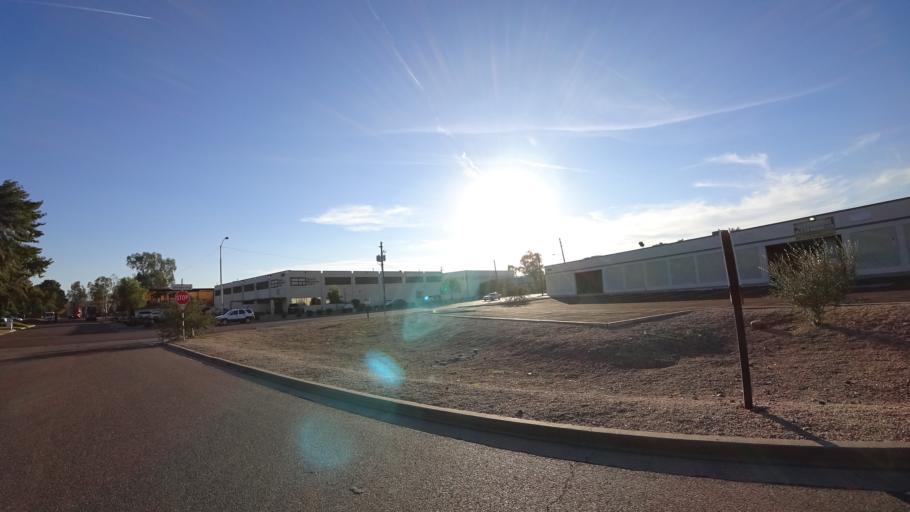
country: US
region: Arizona
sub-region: Maricopa County
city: Phoenix
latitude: 33.4242
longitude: -112.0367
